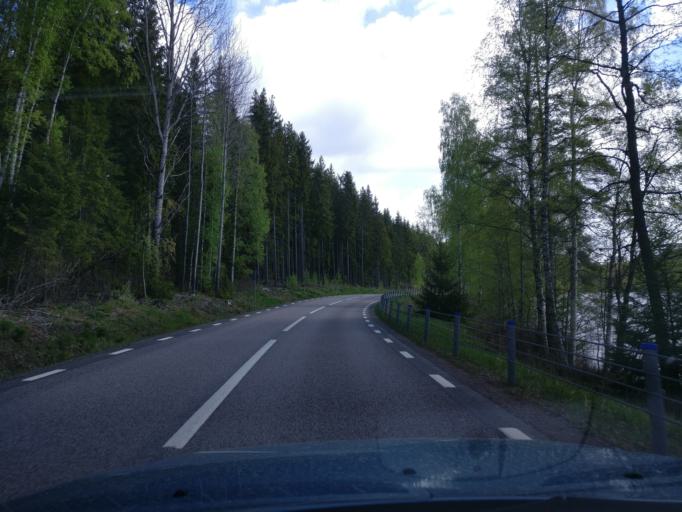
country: SE
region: Vaermland
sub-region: Karlstads Kommun
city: Molkom
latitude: 59.6641
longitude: 13.6988
